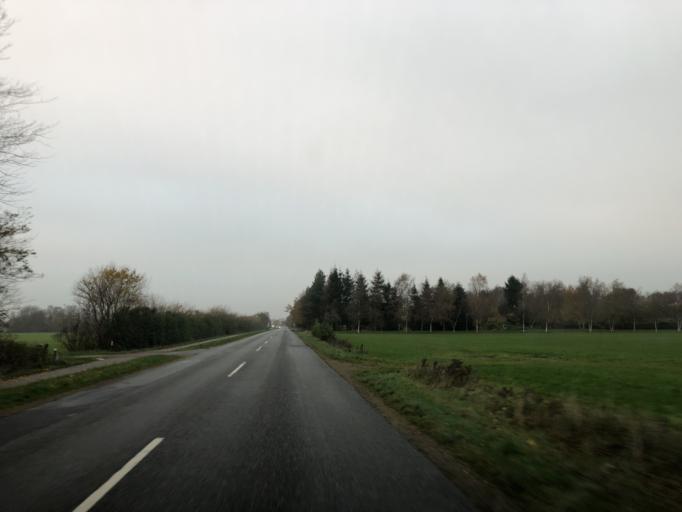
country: DK
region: Central Jutland
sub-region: Herning Kommune
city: Vildbjerg
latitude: 56.2174
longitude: 8.7429
